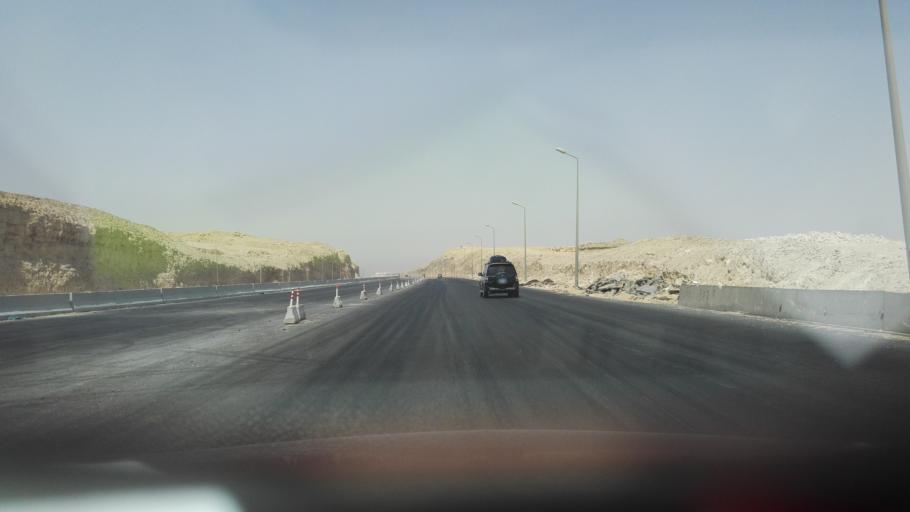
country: EG
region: As Suways
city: Ain Sukhna
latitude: 29.6809
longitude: 32.2179
